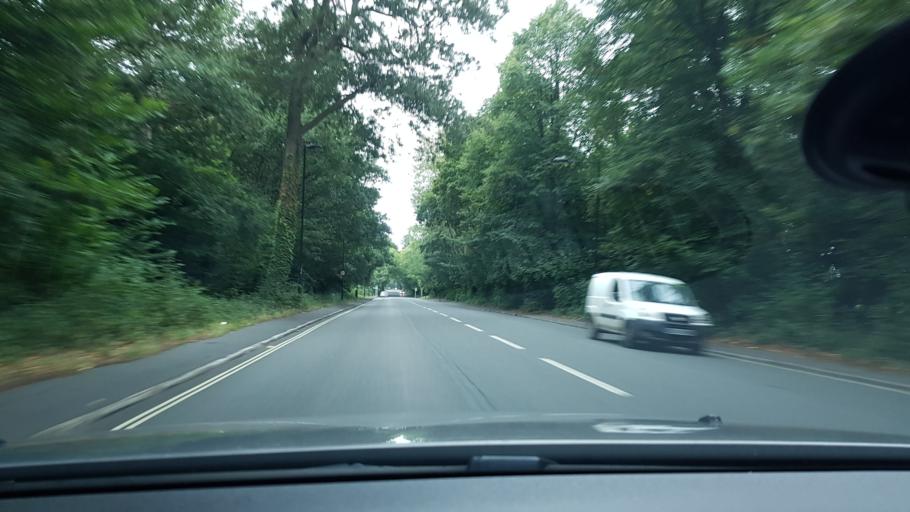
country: GB
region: England
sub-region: Southampton
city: Southampton
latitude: 50.9318
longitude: -1.4060
